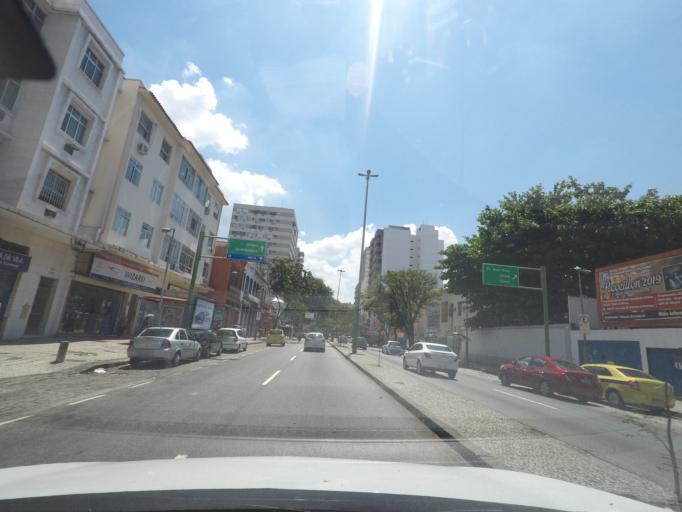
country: BR
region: Rio de Janeiro
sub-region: Rio De Janeiro
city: Rio de Janeiro
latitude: -22.9149
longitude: -43.2412
